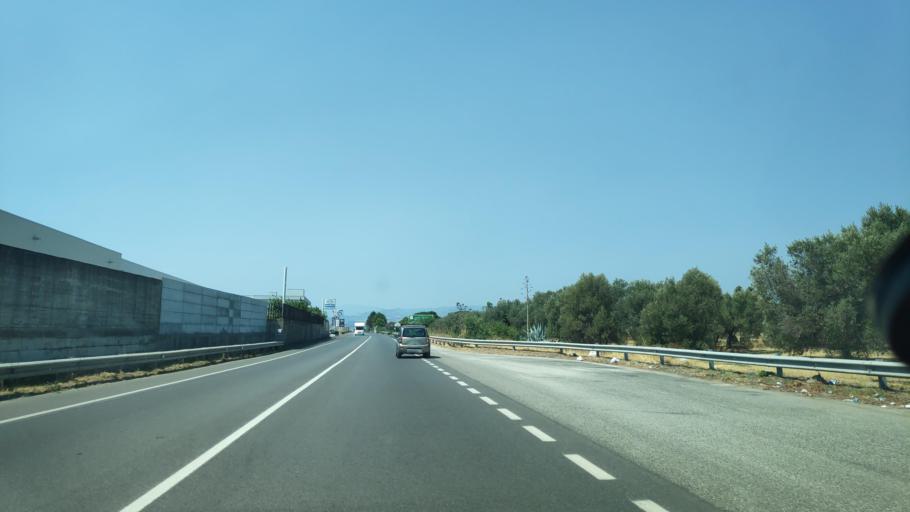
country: IT
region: Calabria
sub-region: Provincia di Reggio Calabria
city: Roccella Ionica
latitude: 38.3081
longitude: 16.3641
